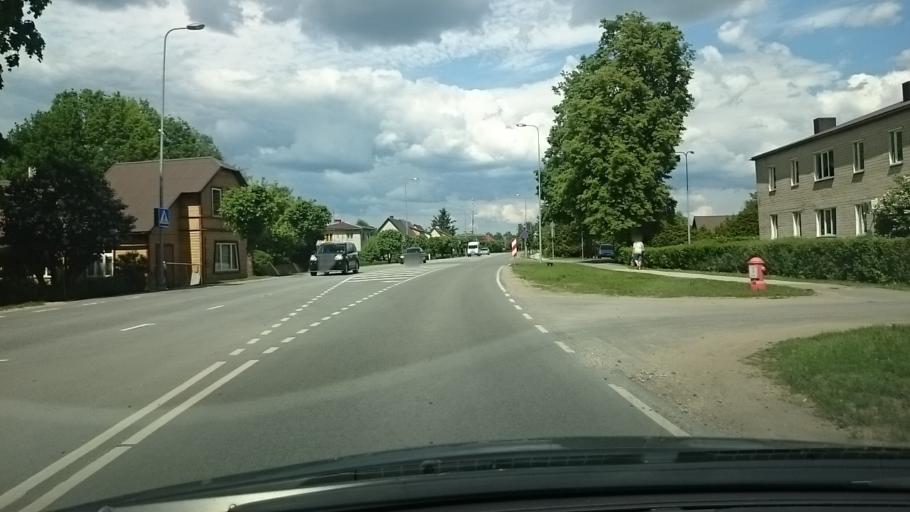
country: EE
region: Jaervamaa
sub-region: Tueri vald
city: Tueri
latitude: 58.8116
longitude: 25.4287
